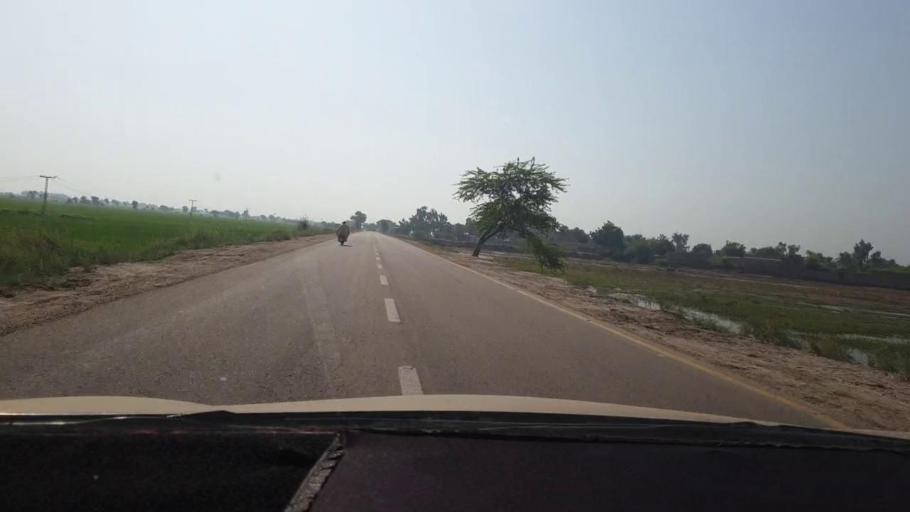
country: PK
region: Sindh
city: Miro Khan
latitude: 27.7245
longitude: 68.1384
